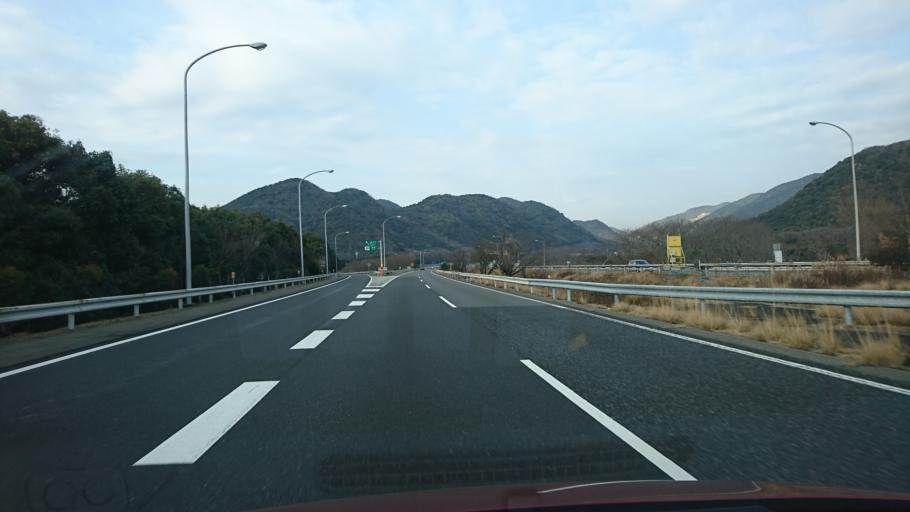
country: JP
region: Hyogo
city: Kariya
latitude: 34.7743
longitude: 134.3762
